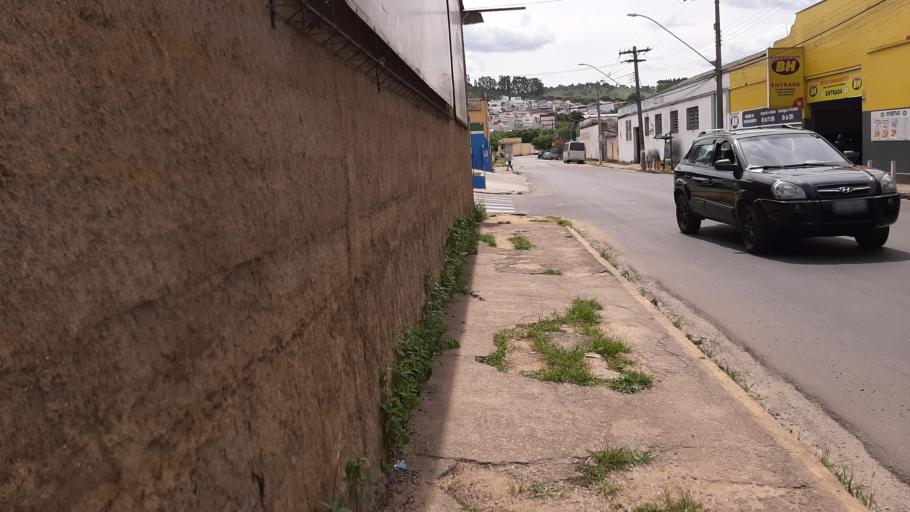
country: BR
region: Minas Gerais
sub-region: Lavras
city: Lavras
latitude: -21.2276
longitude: -45.0025
